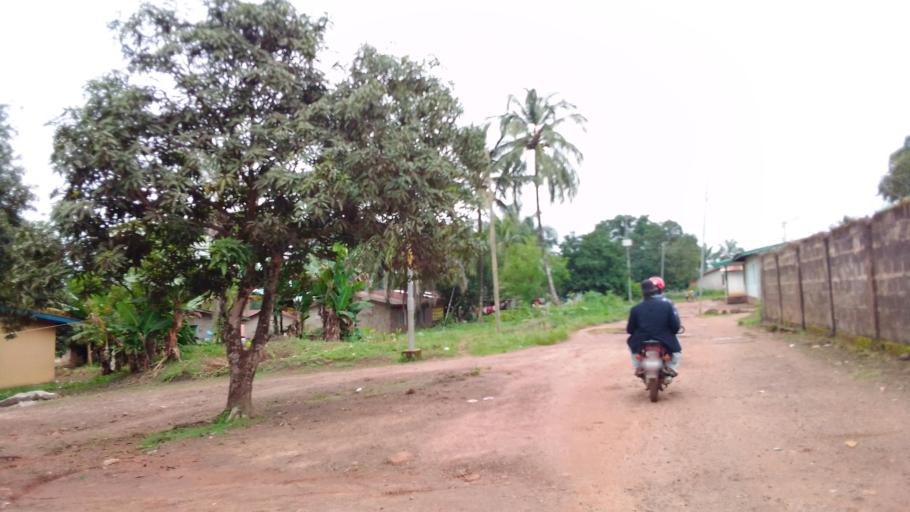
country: SL
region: Eastern Province
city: Kenema
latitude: 7.8611
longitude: -11.2048
